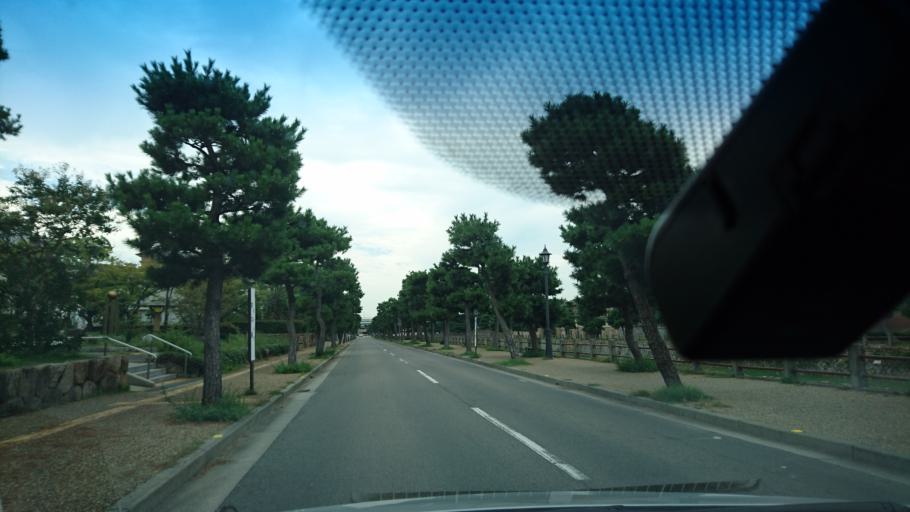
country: JP
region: Hyogo
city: Ashiya
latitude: 34.7312
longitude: 135.3030
